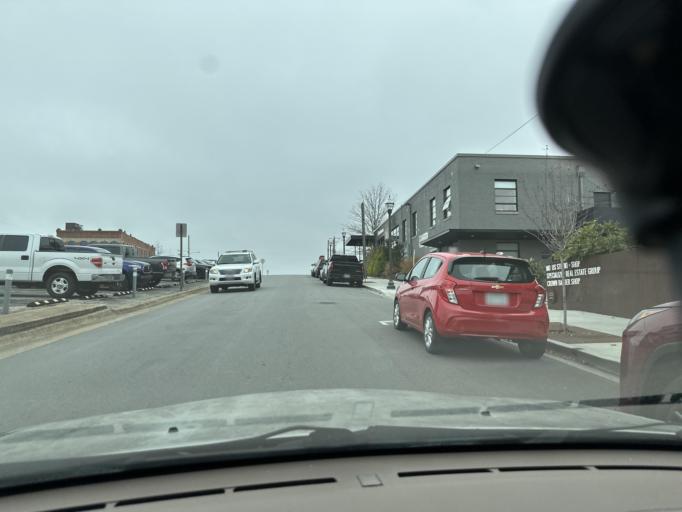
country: US
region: Arkansas
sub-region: Washington County
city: Fayetteville
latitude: 36.0633
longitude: -94.1618
